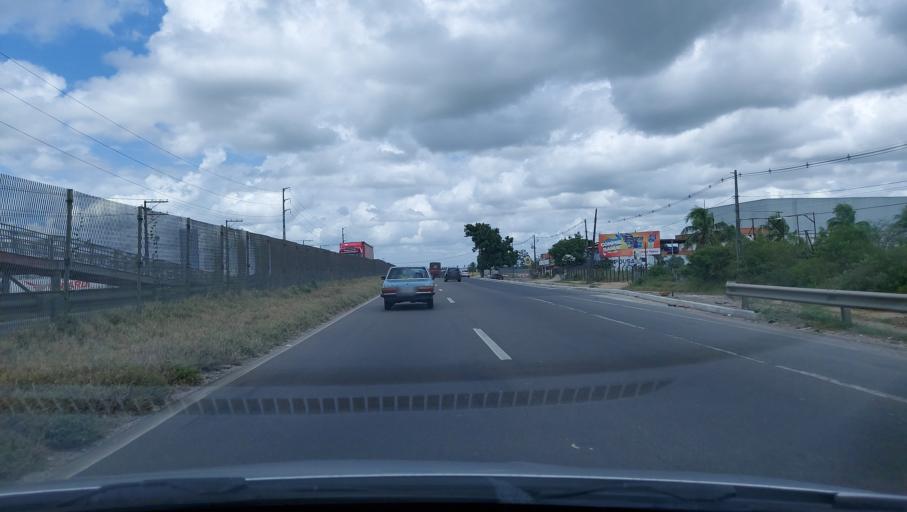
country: BR
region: Bahia
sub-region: Conceicao Do Jacuipe
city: Conceicao do Jacuipe
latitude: -12.3314
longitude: -38.8573
